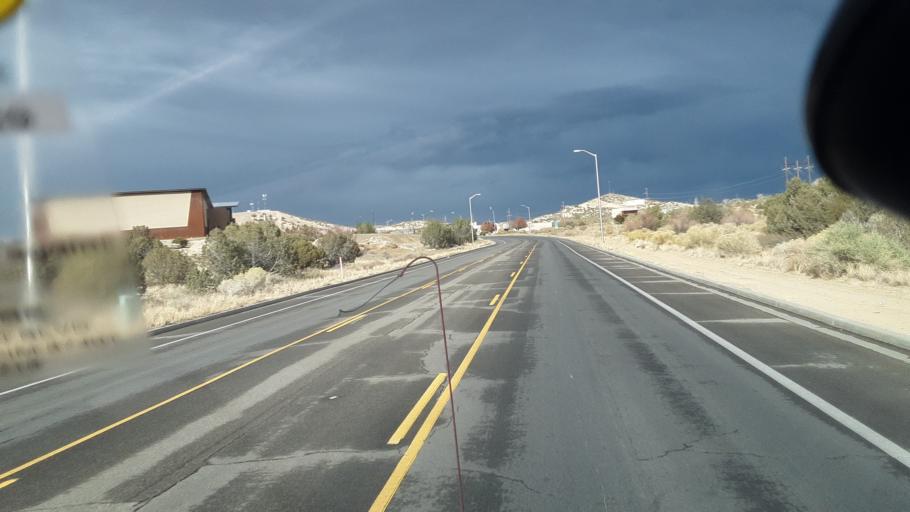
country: US
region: New Mexico
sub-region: San Juan County
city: Farmington
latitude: 36.7671
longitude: -108.1861
